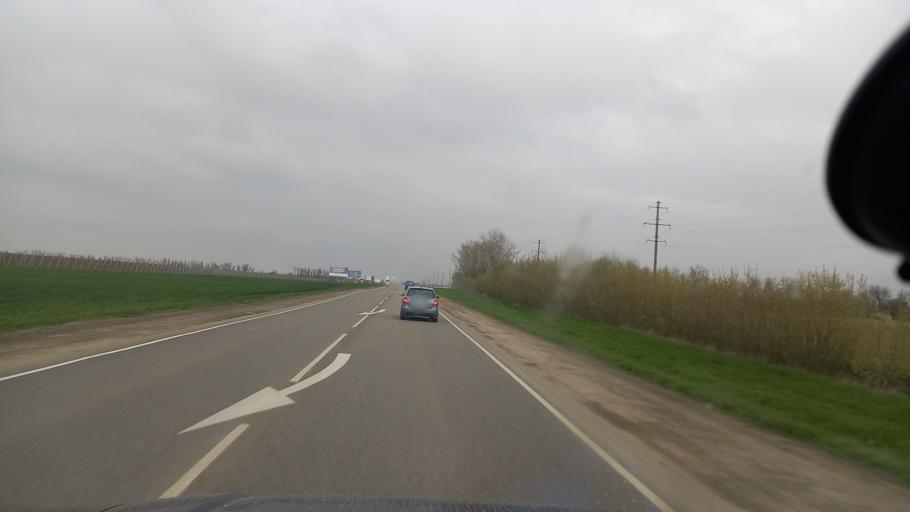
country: RU
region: Krasnodarskiy
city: Slavyansk-na-Kubani
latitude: 45.2446
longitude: 38.0456
